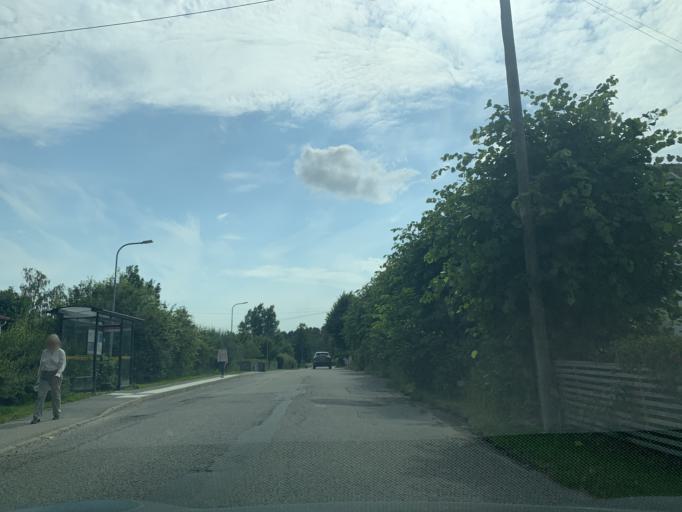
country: SE
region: Stockholm
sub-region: Norrtalje Kommun
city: Bergshamra
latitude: 59.4012
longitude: 18.0171
